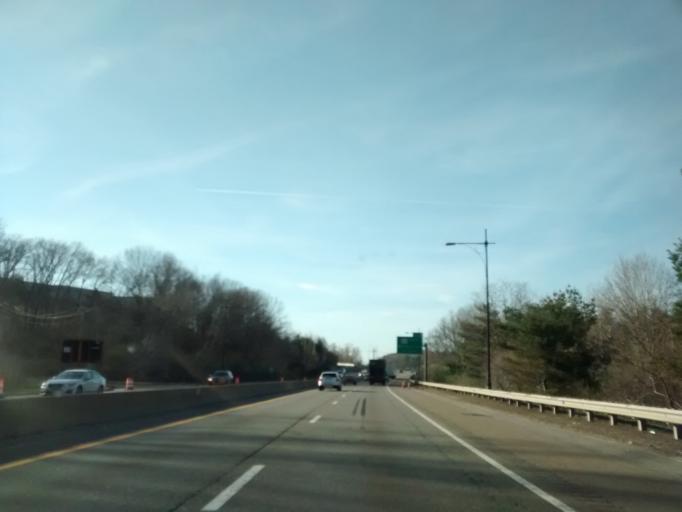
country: US
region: Massachusetts
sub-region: Worcester County
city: Millbury
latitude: 42.1958
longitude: -71.7728
